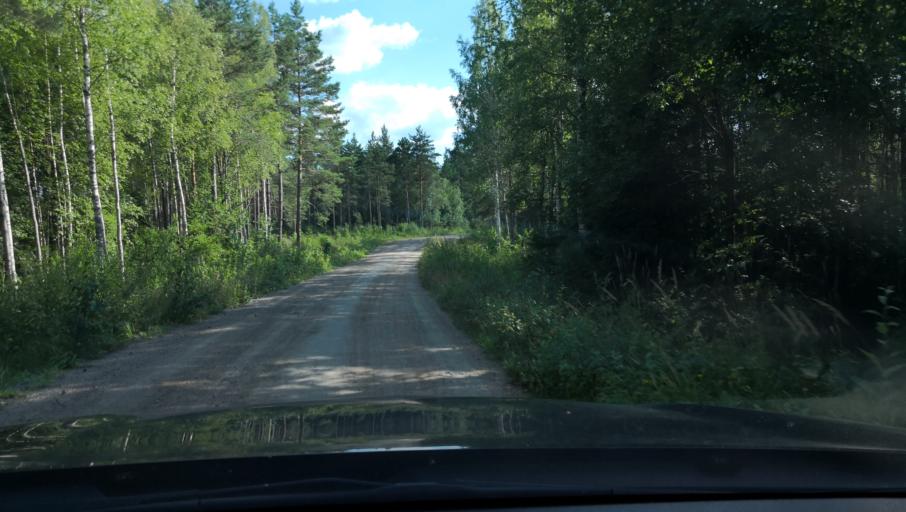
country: SE
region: Vaestmanland
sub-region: Vasteras
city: Skultuna
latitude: 59.7174
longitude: 16.3725
